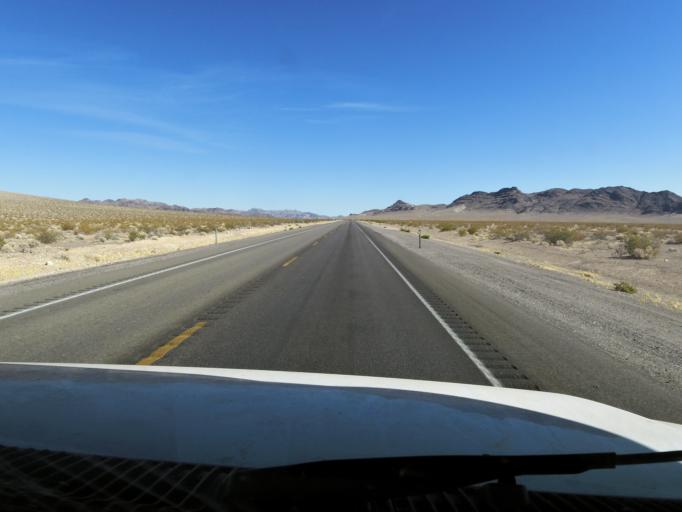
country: US
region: Nevada
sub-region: Nye County
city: Beatty
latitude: 36.6344
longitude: -116.3611
